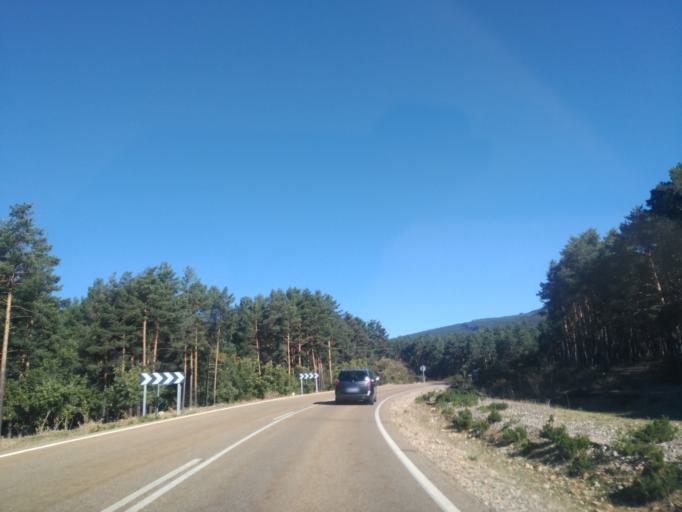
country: ES
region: Castille and Leon
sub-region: Provincia de Soria
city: Vinuesa
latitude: 41.9492
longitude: -2.7738
